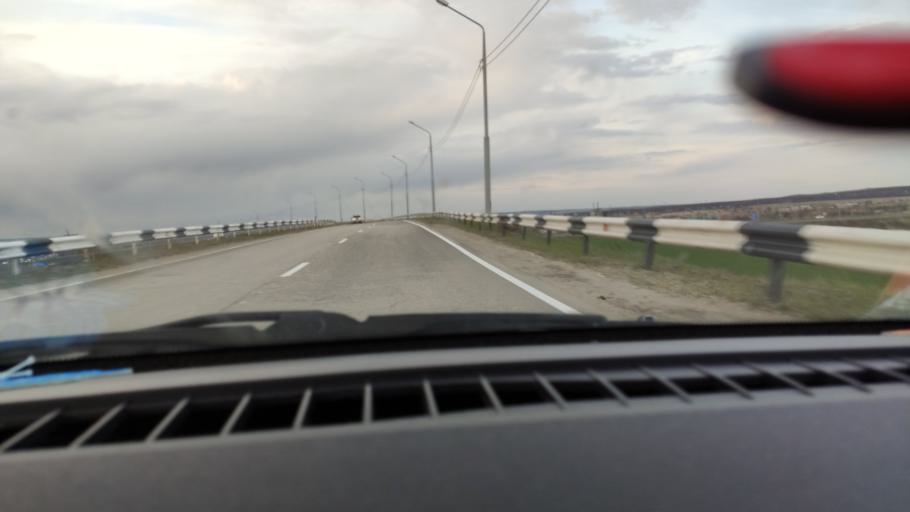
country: RU
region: Saratov
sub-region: Saratovskiy Rayon
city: Saratov
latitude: 51.6713
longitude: 46.0013
